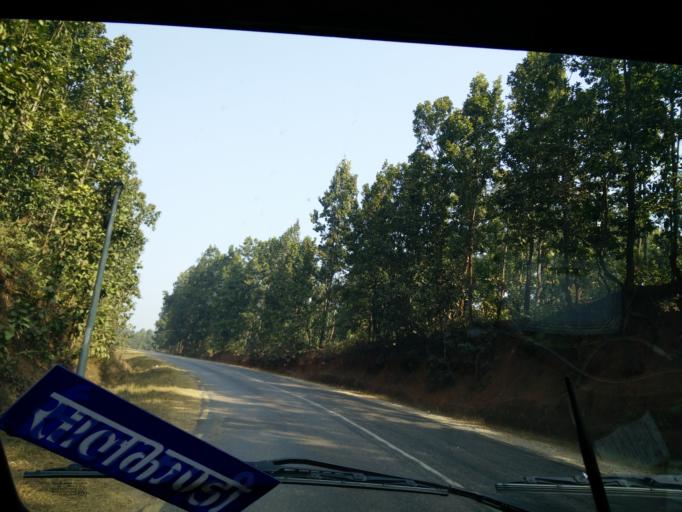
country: NP
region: Central Region
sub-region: Narayani Zone
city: Bharatpur
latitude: 27.6183
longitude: 84.0257
